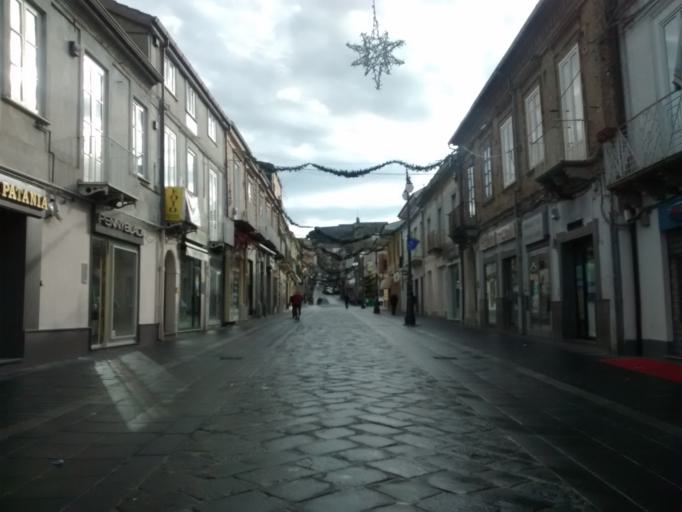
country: IT
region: Calabria
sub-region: Provincia di Vibo-Valentia
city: Vibo Valentia
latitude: 38.6738
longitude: 16.1012
